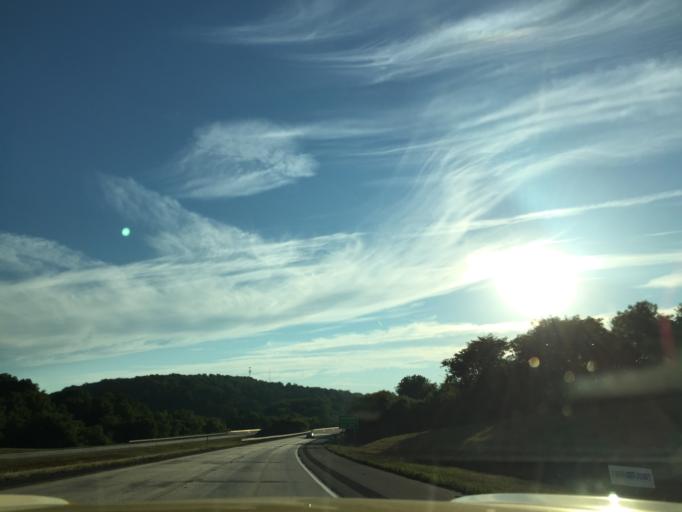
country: US
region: Pennsylvania
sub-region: Berks County
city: Kutztown
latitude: 40.5245
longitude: -75.7864
